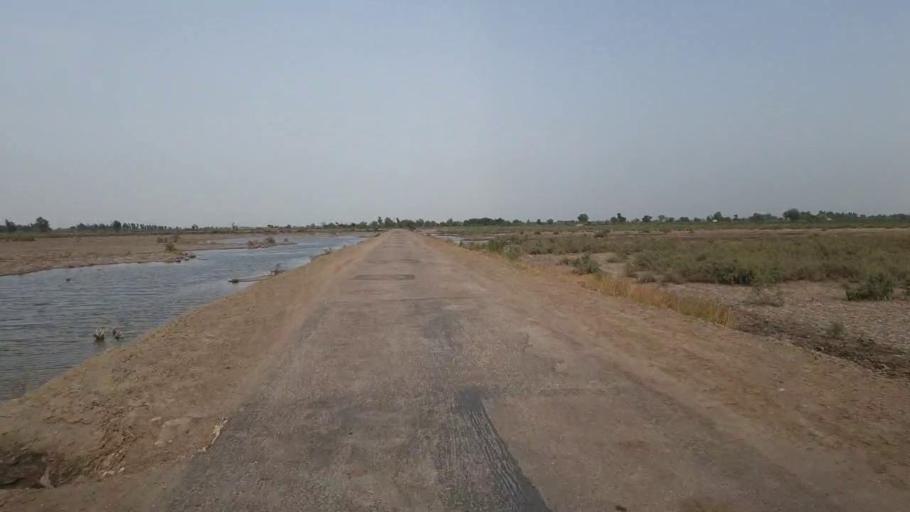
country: PK
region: Sindh
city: Daulatpur
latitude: 26.5462
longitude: 68.0842
